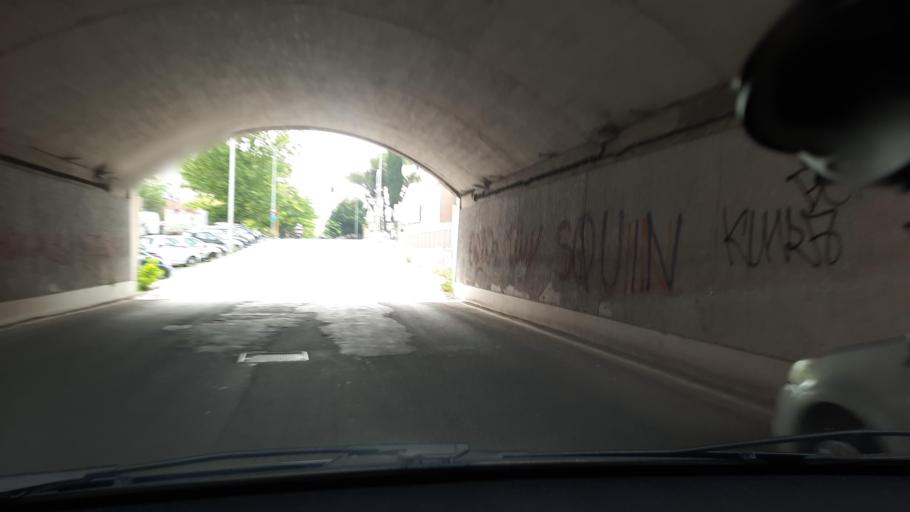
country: IT
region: Latium
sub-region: Citta metropolitana di Roma Capitale
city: Rome
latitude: 41.8568
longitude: 12.4785
